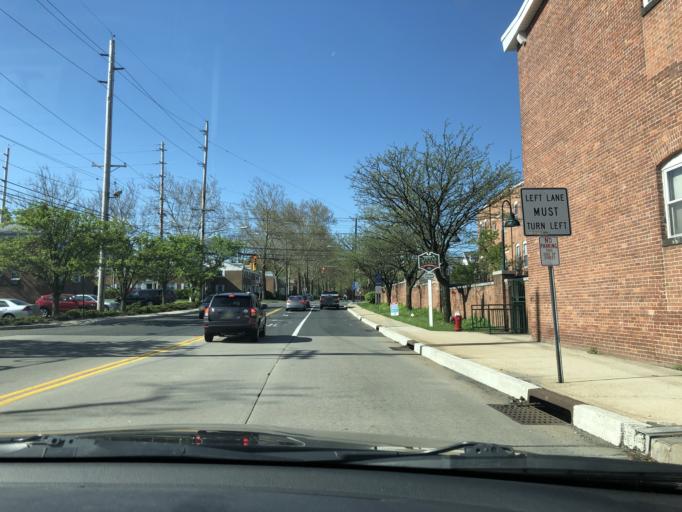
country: US
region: New Jersey
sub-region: Passaic County
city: Singac
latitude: 40.8835
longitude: -74.2331
